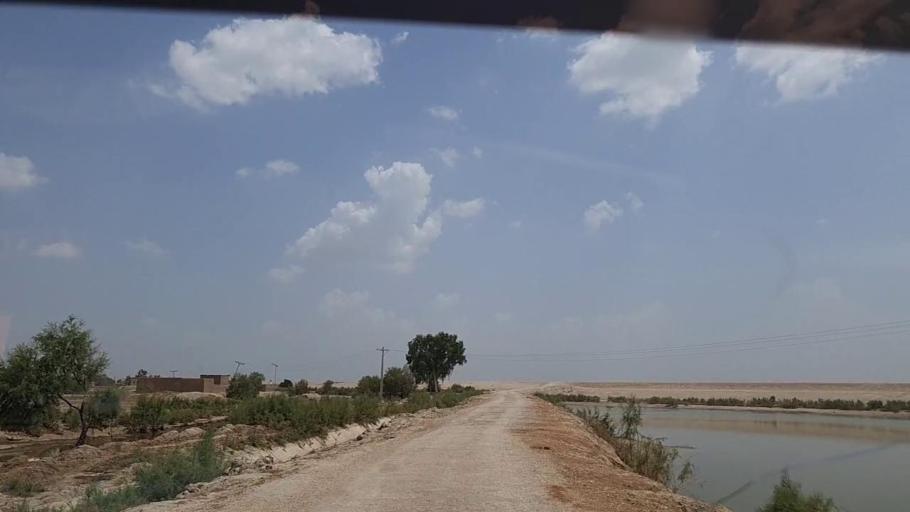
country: PK
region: Sindh
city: Bhan
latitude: 26.5030
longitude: 67.6402
